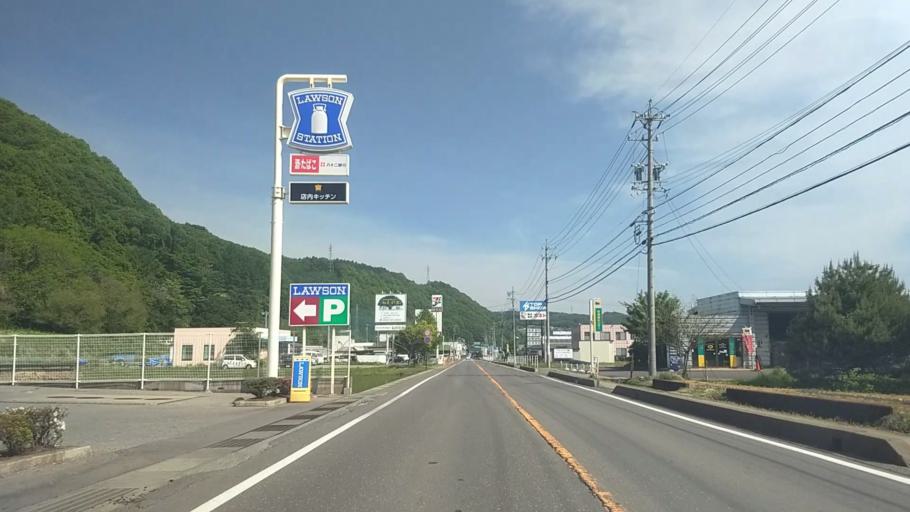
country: JP
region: Nagano
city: Saku
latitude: 36.1166
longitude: 138.4723
